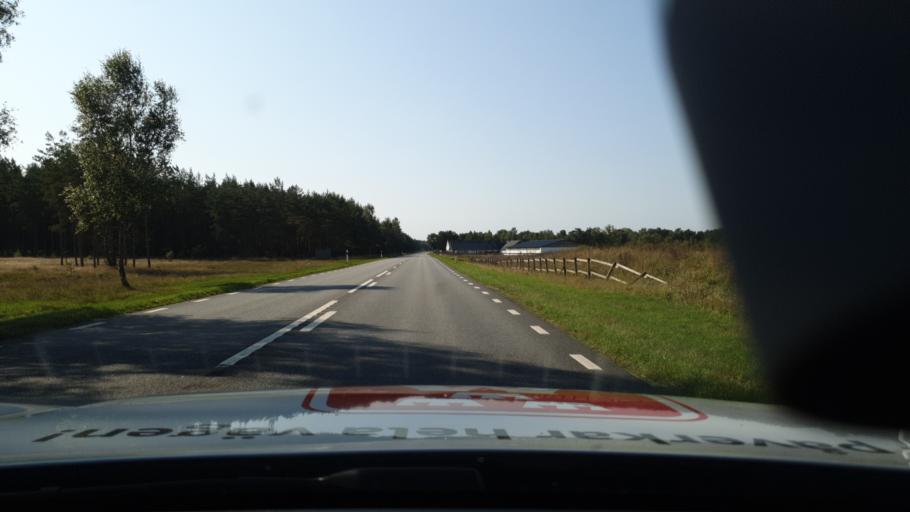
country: SE
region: Skane
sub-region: Kristianstads Kommun
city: Ahus
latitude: 55.8988
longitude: 14.2565
